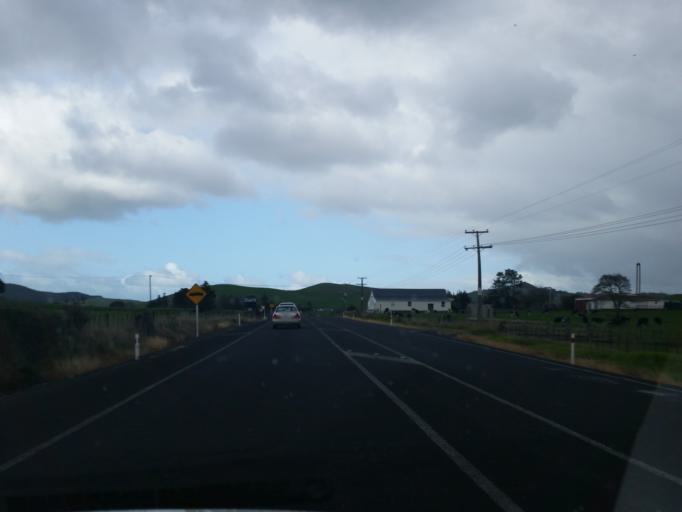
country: NZ
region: Waikato
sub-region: Waikato District
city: Te Kauwhata
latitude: -37.2517
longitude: 175.2316
